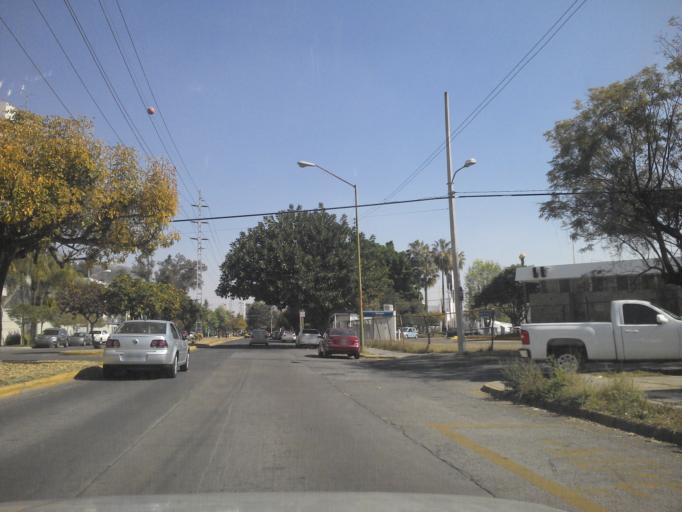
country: MX
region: Jalisco
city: Guadalajara
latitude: 20.6872
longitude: -103.3814
